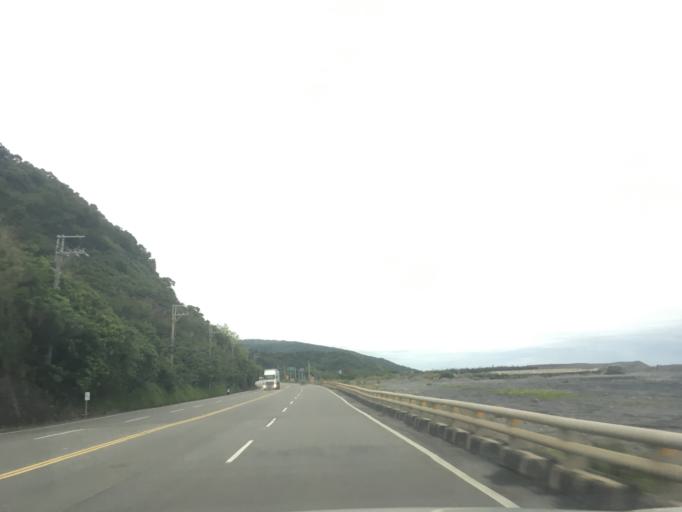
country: TW
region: Taiwan
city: Hengchun
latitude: 22.3328
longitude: 120.8935
